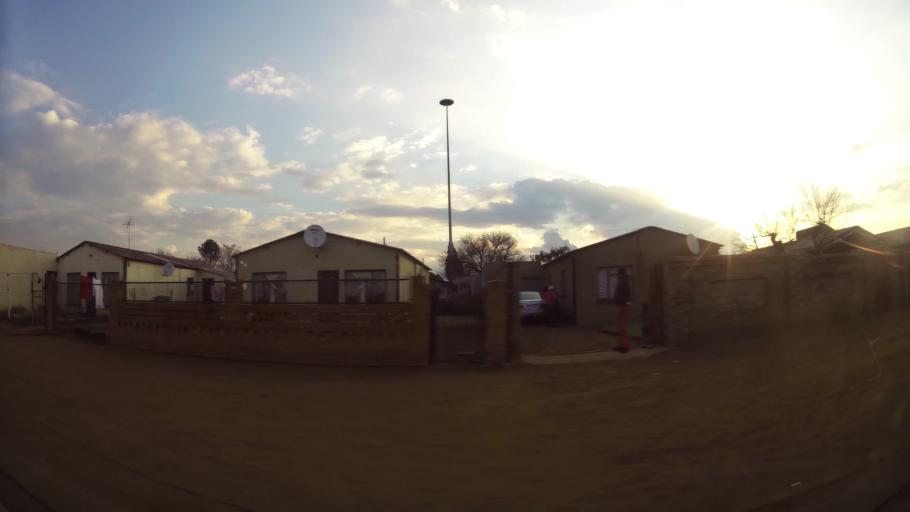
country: ZA
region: Gauteng
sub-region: City of Johannesburg Metropolitan Municipality
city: Orange Farm
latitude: -26.5489
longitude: 27.8637
